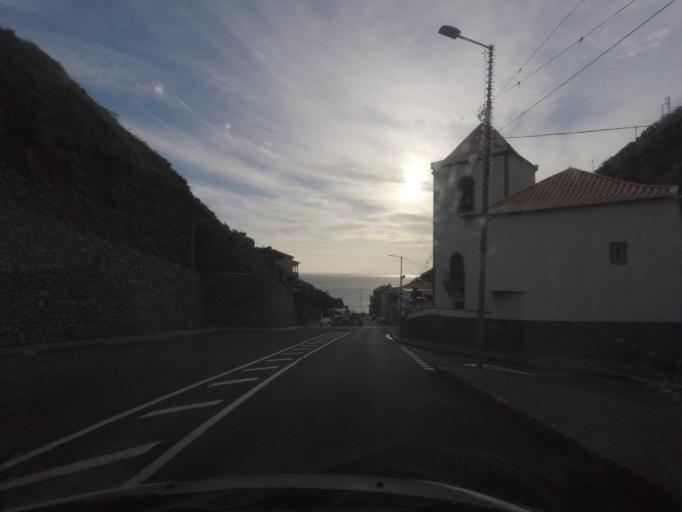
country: PT
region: Madeira
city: Calheta
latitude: 32.7231
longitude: -17.1767
